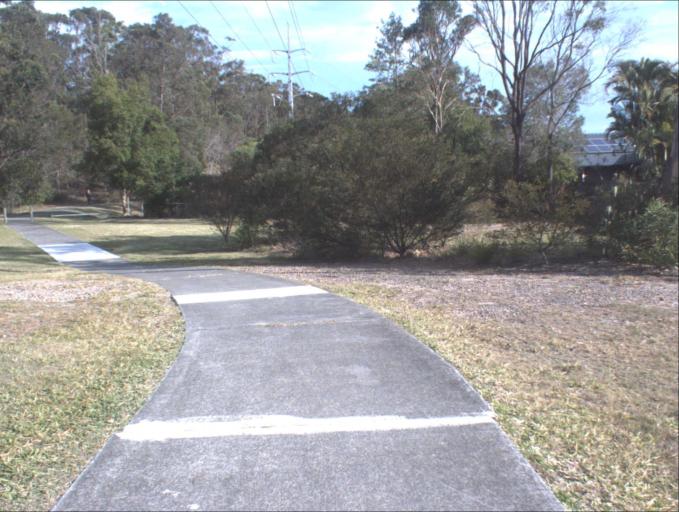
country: AU
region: Queensland
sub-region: Logan
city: Slacks Creek
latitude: -27.6290
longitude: 153.1465
